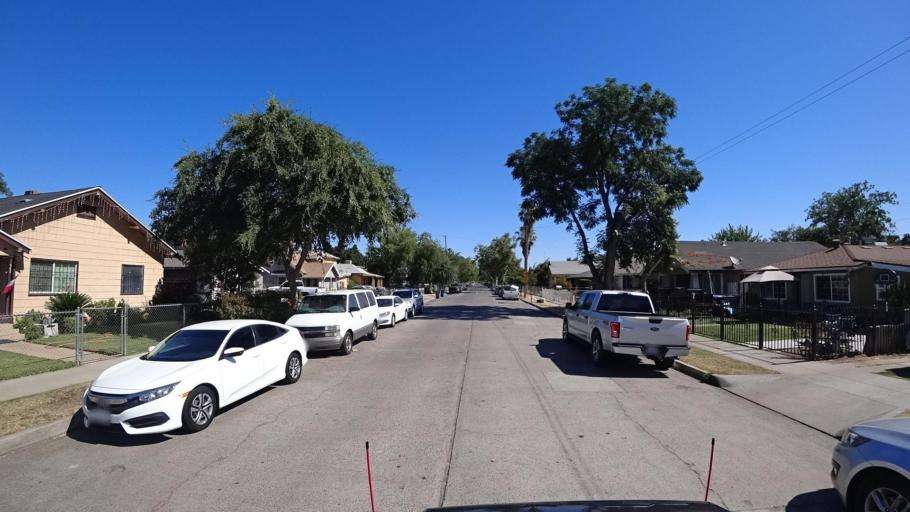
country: US
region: California
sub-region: Fresno County
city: Fresno
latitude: 36.7511
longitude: -119.8052
